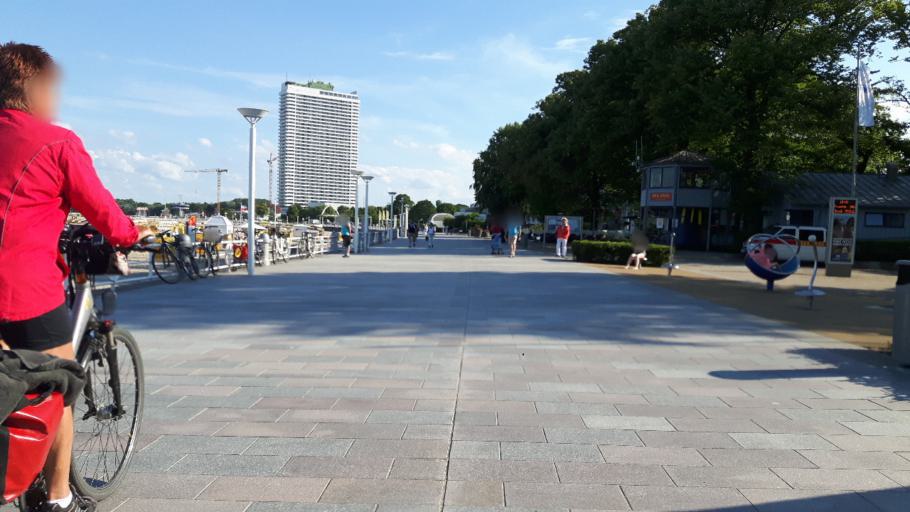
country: DE
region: Schleswig-Holstein
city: Travemuende
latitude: 53.9676
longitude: 10.8810
